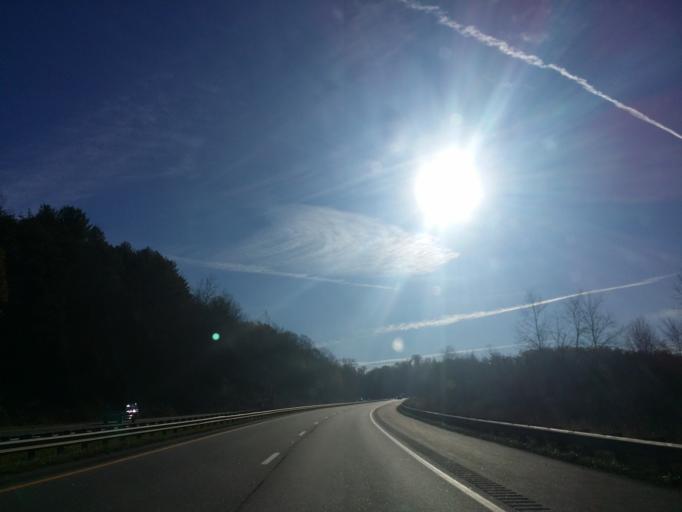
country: US
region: North Carolina
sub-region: McDowell County
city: West Marion
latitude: 35.6399
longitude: -82.1125
